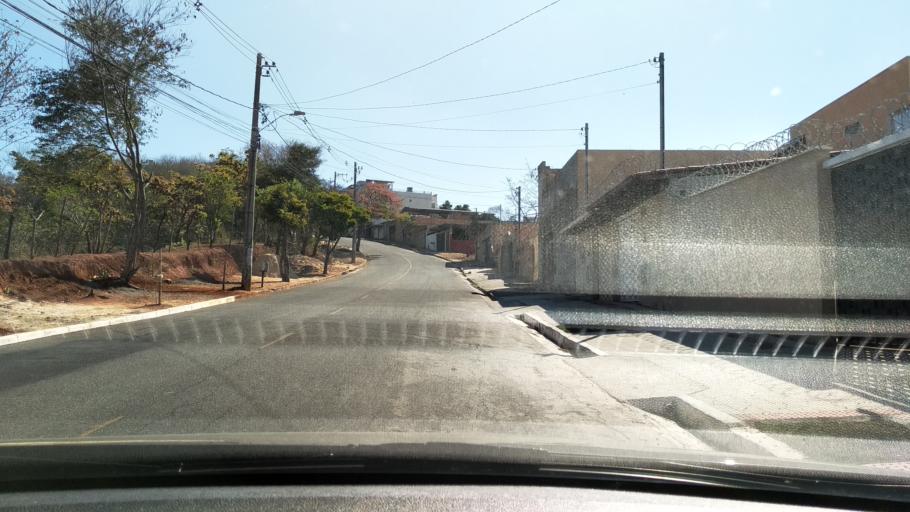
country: BR
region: Minas Gerais
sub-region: Belo Horizonte
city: Belo Horizonte
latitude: -19.8620
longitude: -43.8785
